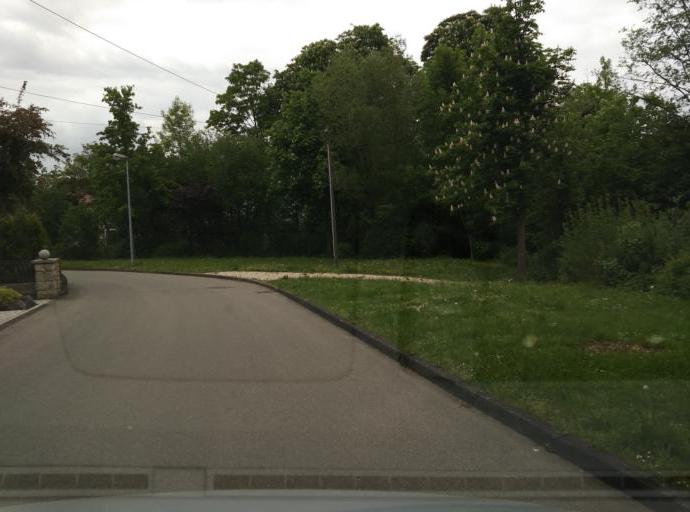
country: DE
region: Baden-Wuerttemberg
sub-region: Regierungsbezirk Stuttgart
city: Frickenhausen
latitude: 48.5895
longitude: 9.3608
